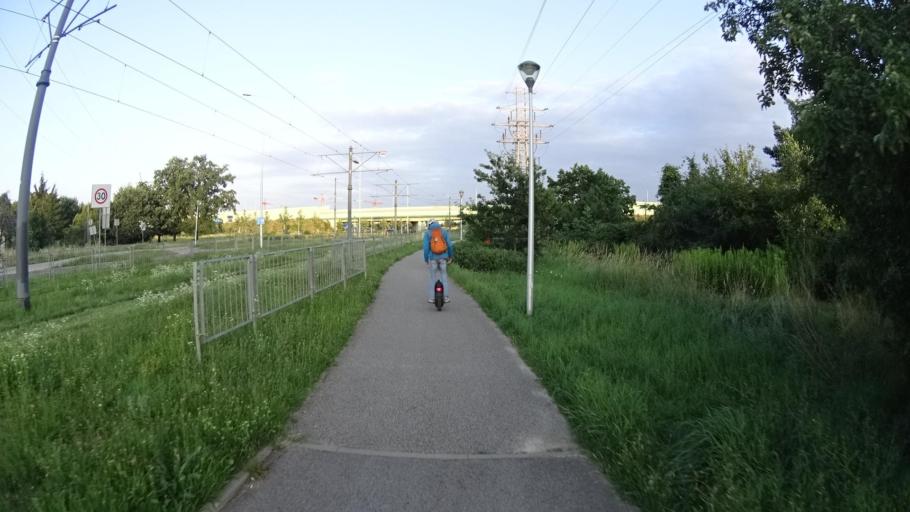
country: PL
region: Masovian Voivodeship
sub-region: Warszawa
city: Bialoleka
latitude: 52.3155
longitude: 20.9666
